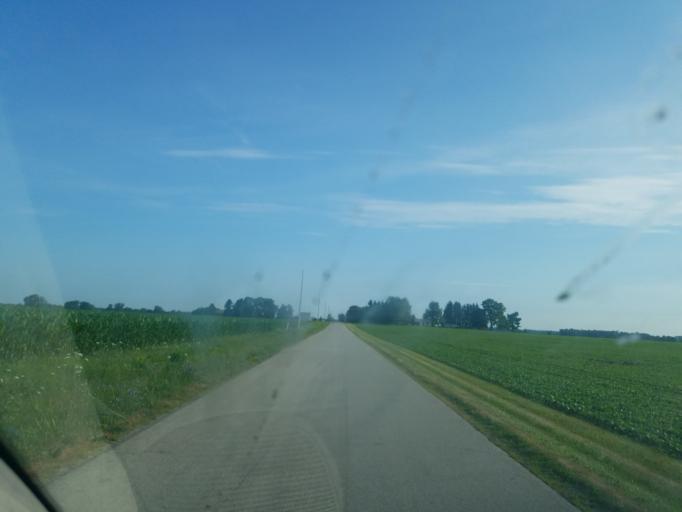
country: US
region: Ohio
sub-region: Wyandot County
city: Upper Sandusky
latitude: 40.7422
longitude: -83.1689
